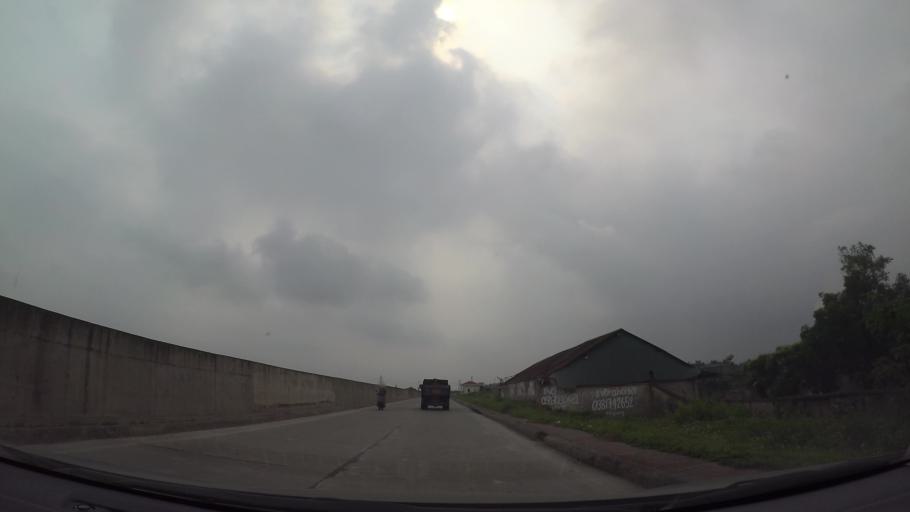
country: VN
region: Ha Noi
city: Trau Quy
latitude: 21.0760
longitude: 105.9117
